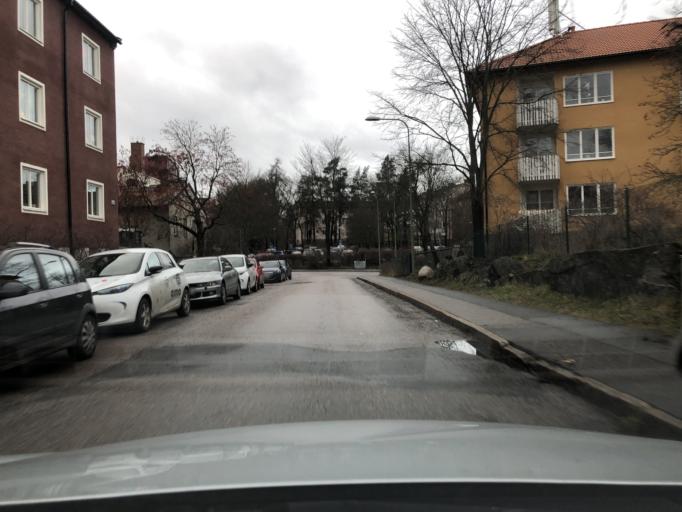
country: SE
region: Stockholm
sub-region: Stockholms Kommun
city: Arsta
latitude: 59.3001
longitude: 18.0442
